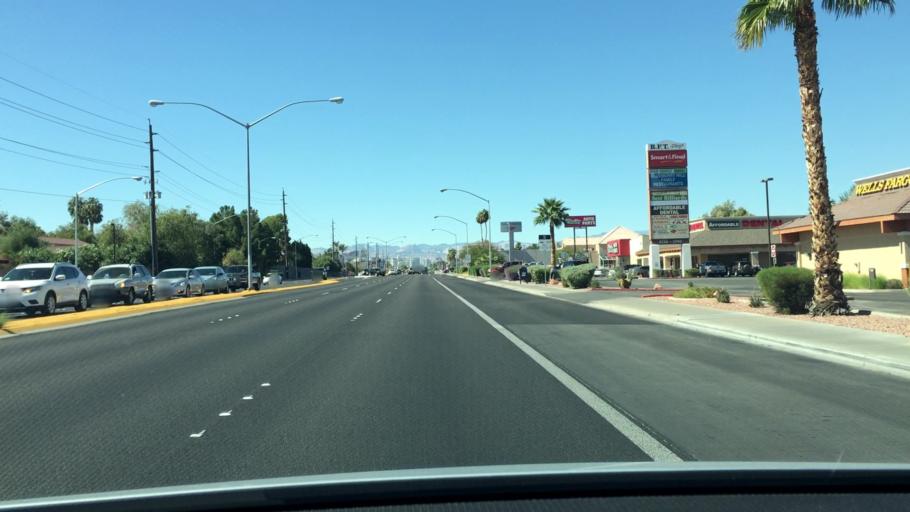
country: US
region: Nevada
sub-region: Clark County
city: Winchester
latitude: 36.1154
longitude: -115.0925
